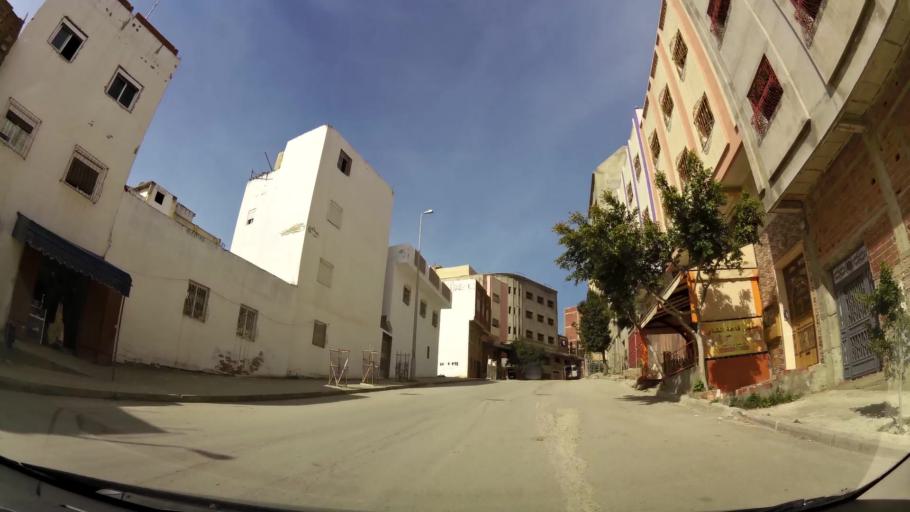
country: MA
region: Tanger-Tetouan
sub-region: Tanger-Assilah
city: Tangier
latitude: 35.7242
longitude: -5.8118
